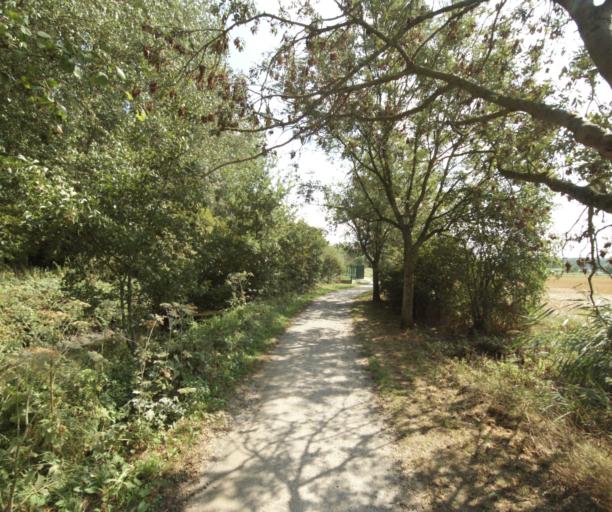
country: FR
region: Nord-Pas-de-Calais
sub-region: Departement du Nord
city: Hem
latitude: 50.6441
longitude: 3.1825
